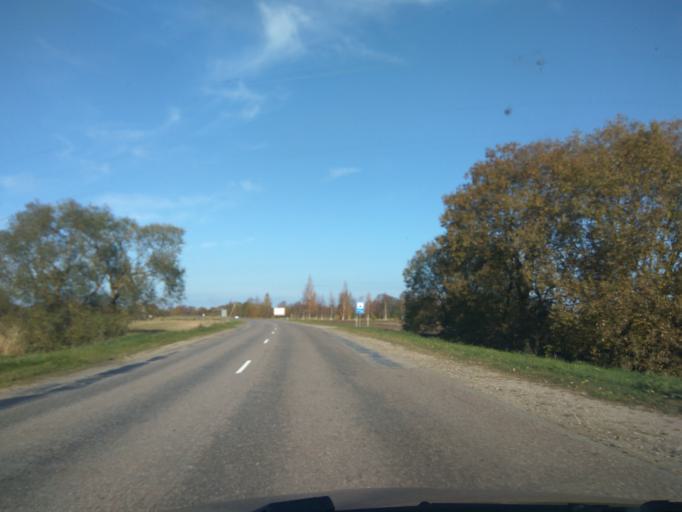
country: LV
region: Ventspils
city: Ventspils
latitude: 57.3243
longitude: 21.5636
